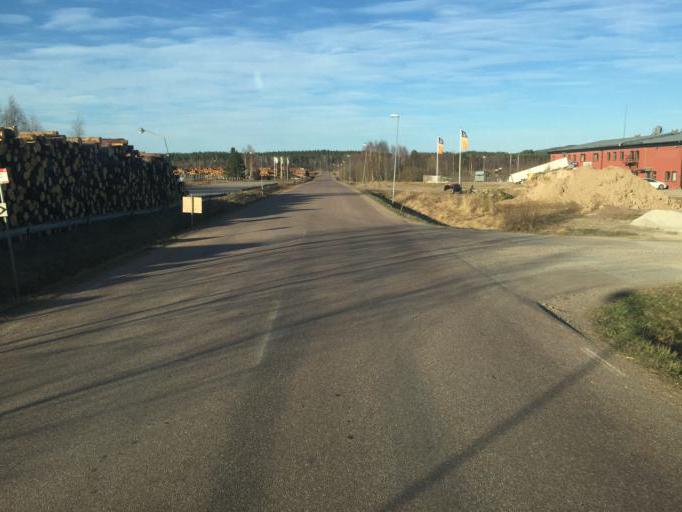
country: SE
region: Dalarna
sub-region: Gagnefs Kommun
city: Mockfjard
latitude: 60.4946
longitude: 14.9670
